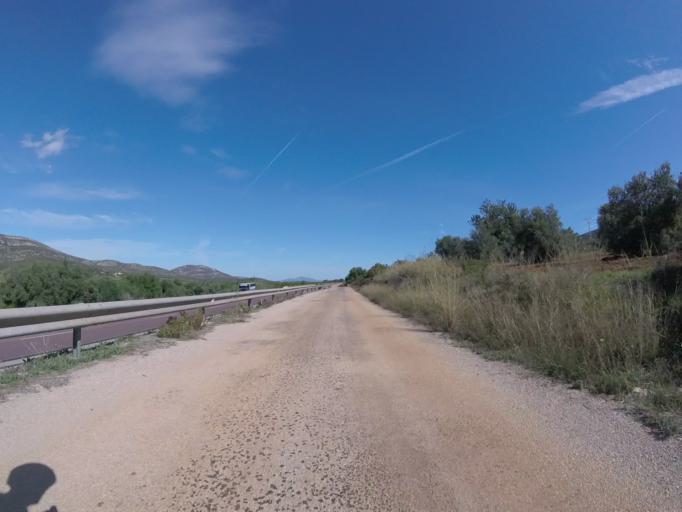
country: ES
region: Valencia
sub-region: Provincia de Castello
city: Santa Magdalena de Pulpis
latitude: 40.3743
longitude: 0.3289
